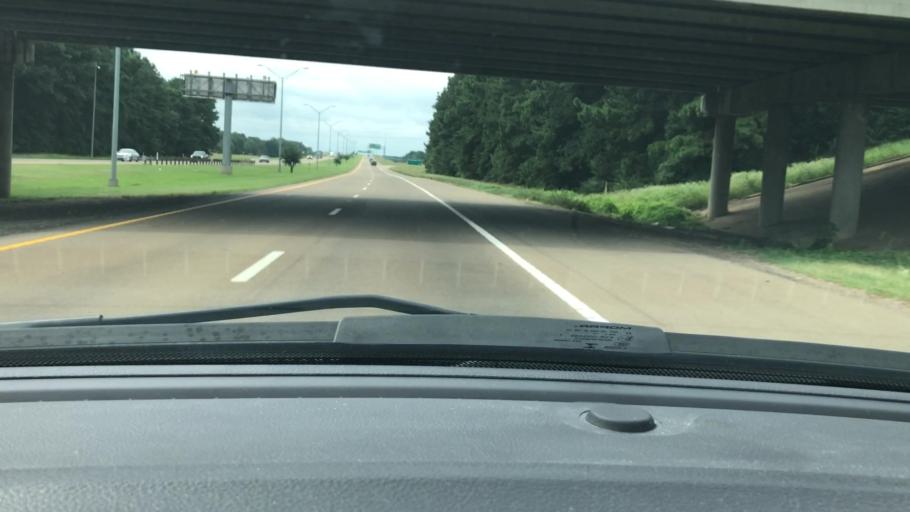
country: US
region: Texas
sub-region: Bowie County
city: Wake Village
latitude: 33.4120
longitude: -94.0975
